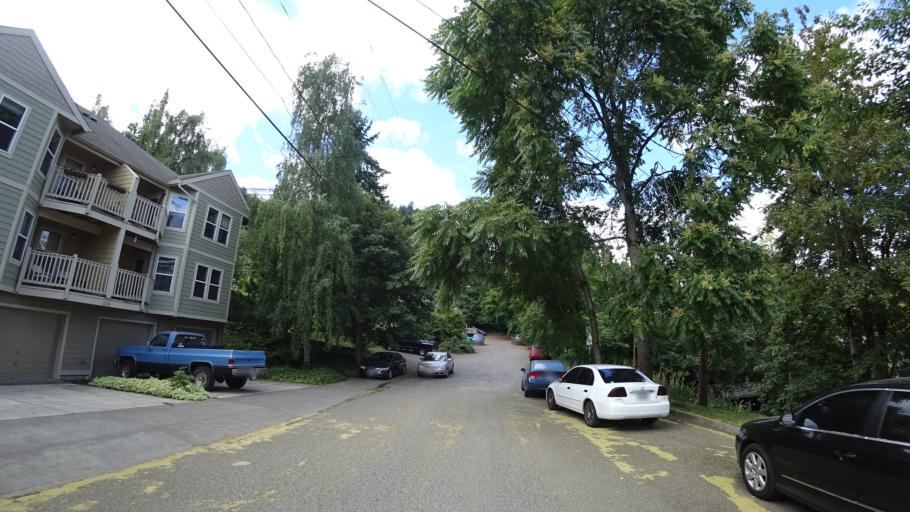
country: US
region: Oregon
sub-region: Multnomah County
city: Portland
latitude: 45.5030
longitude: -122.6806
